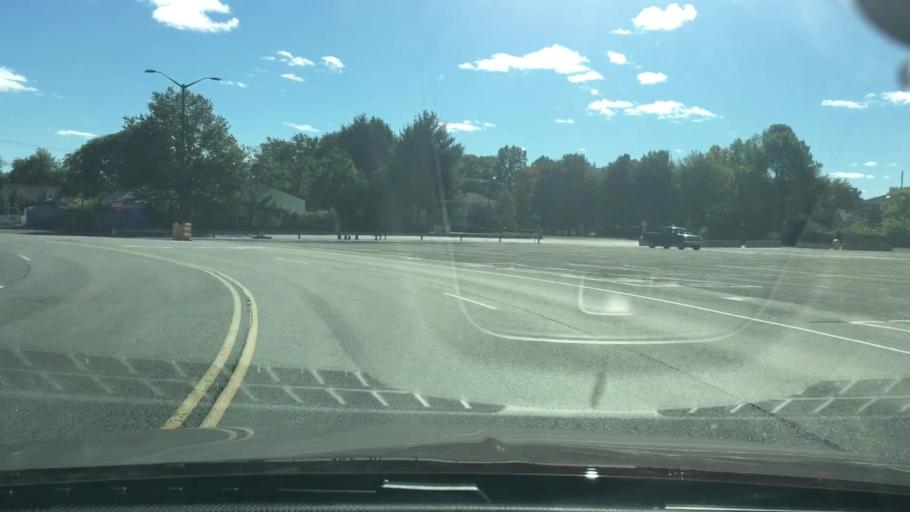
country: US
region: Connecticut
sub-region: Hartford County
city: Wethersfield
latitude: 41.7447
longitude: -72.6302
